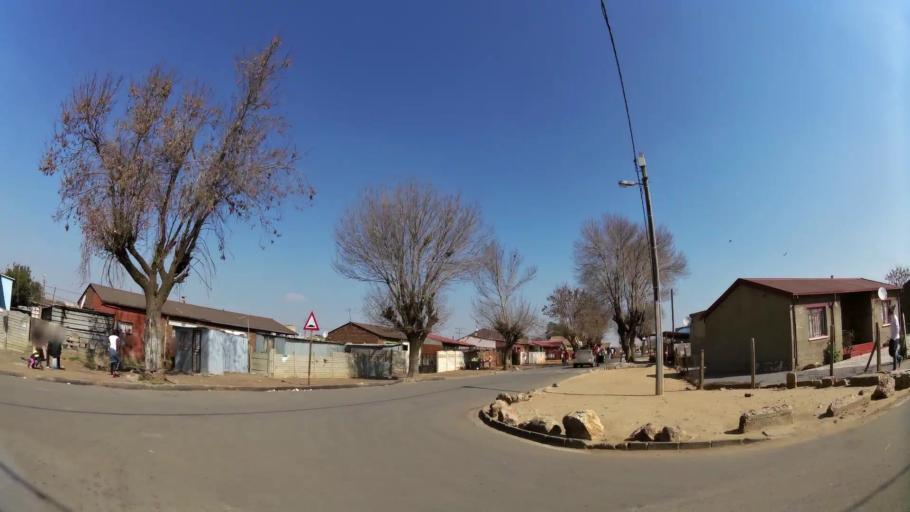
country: ZA
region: Gauteng
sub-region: Ekurhuleni Metropolitan Municipality
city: Boksburg
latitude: -26.2165
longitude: 28.2962
